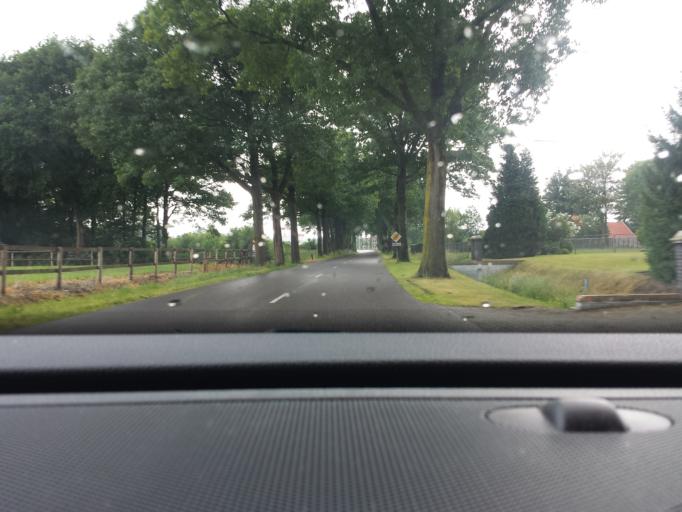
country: NL
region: Gelderland
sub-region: Berkelland
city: Eibergen
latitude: 52.0515
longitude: 6.6293
